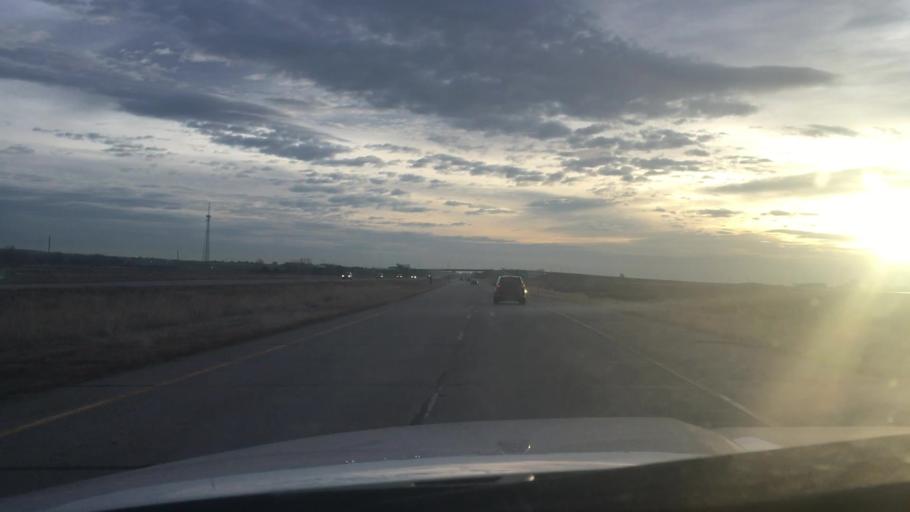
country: US
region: Colorado
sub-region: Morgan County
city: Fort Morgan
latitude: 40.2423
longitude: -103.9376
